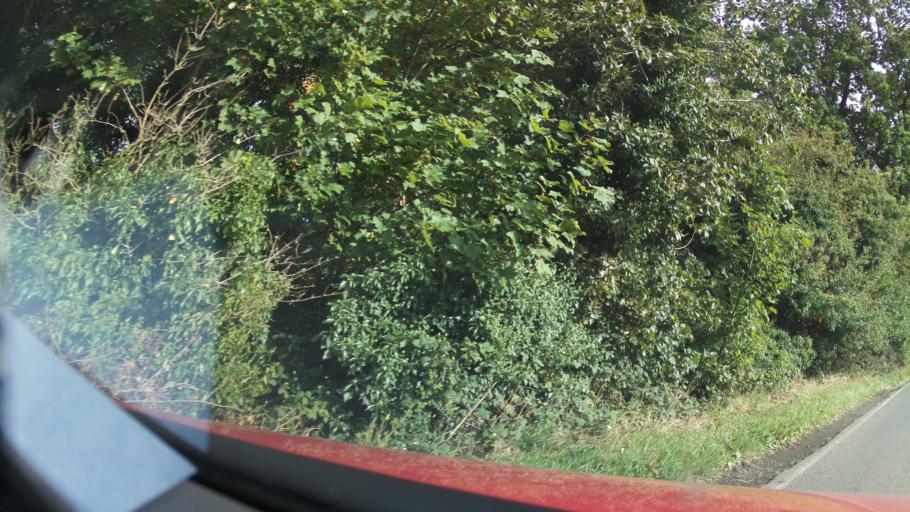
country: GB
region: England
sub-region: Telford and Wrekin
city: Madeley
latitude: 52.6261
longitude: -2.4130
